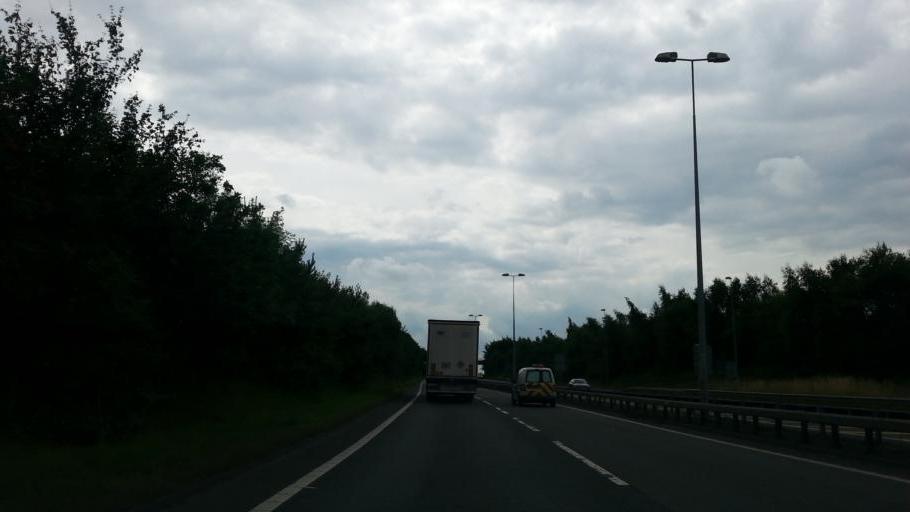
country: GB
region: England
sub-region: Warwickshire
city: Curdworth
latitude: 52.5661
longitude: -1.7699
